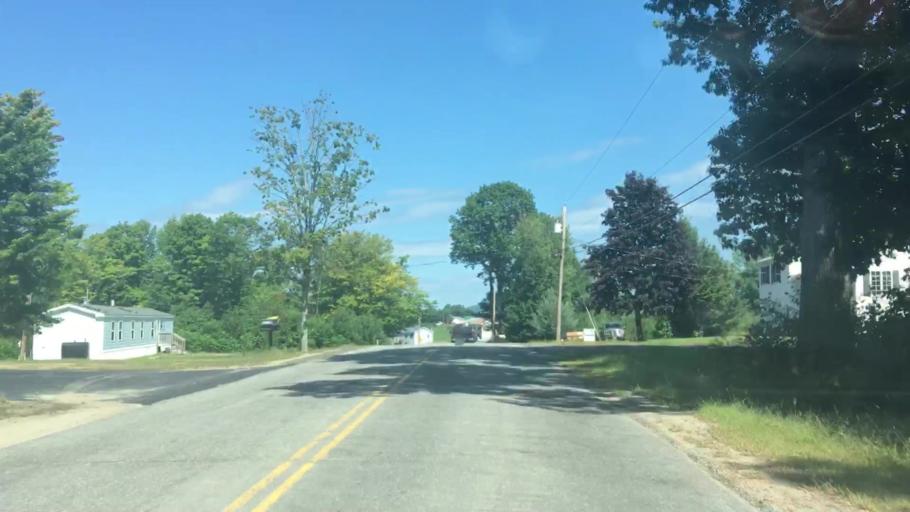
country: US
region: Maine
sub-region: Androscoggin County
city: Lisbon
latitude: 44.0670
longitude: -70.1143
